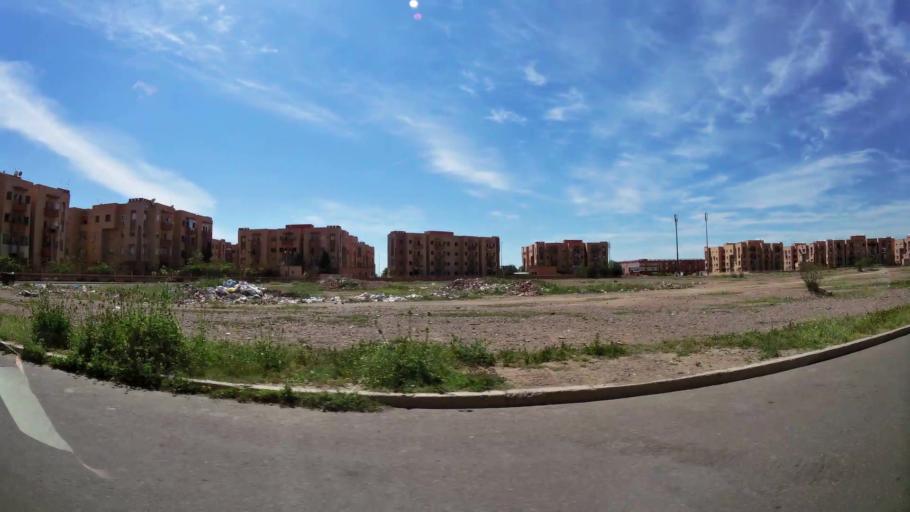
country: MA
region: Marrakech-Tensift-Al Haouz
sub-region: Marrakech
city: Marrakesh
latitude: 31.6429
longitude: -8.0790
